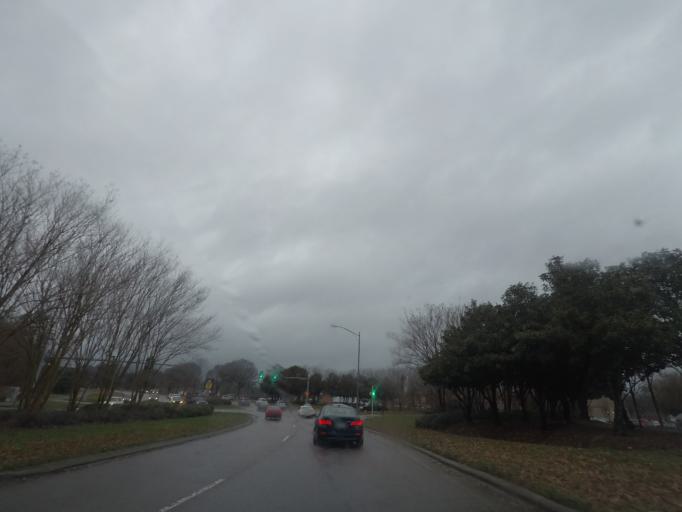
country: US
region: North Carolina
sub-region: Durham County
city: Durham
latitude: 35.9030
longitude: -78.9444
